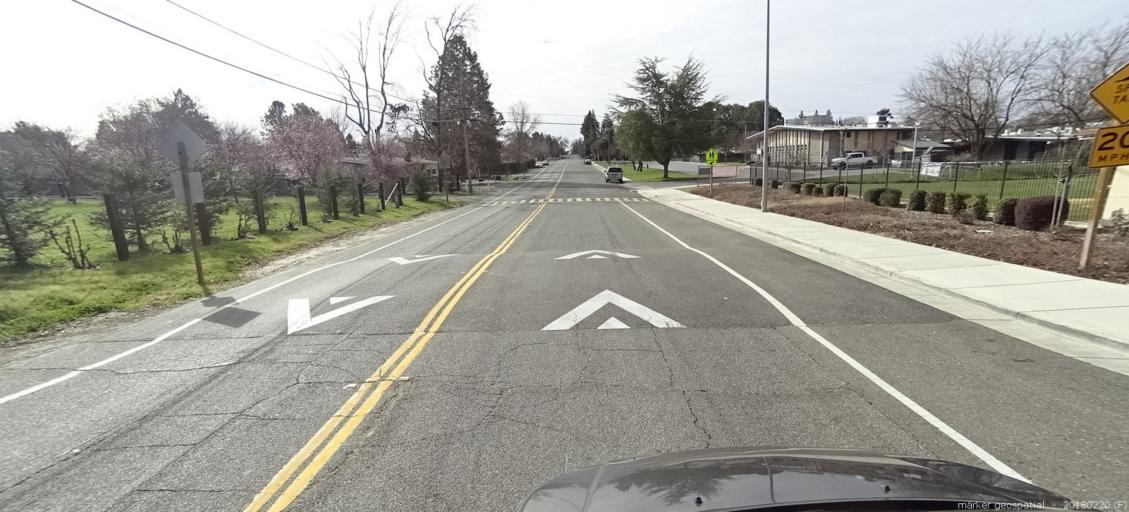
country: US
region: California
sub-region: Sacramento County
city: Orangevale
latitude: 38.6990
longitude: -121.2300
